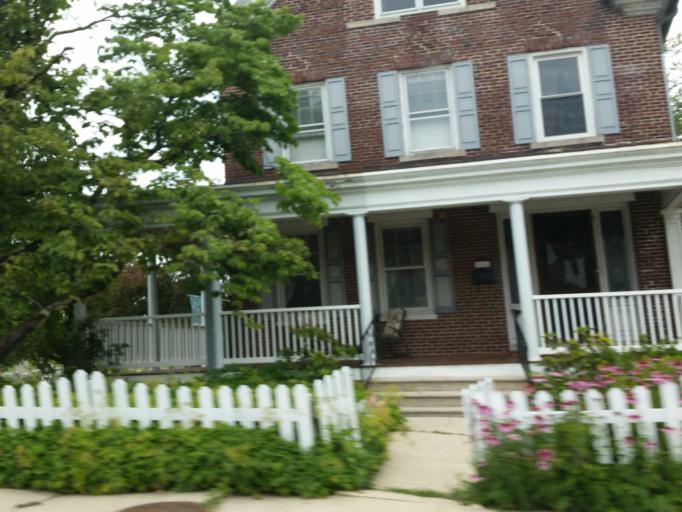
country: US
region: Pennsylvania
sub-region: York County
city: North York
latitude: 39.9760
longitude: -76.7328
